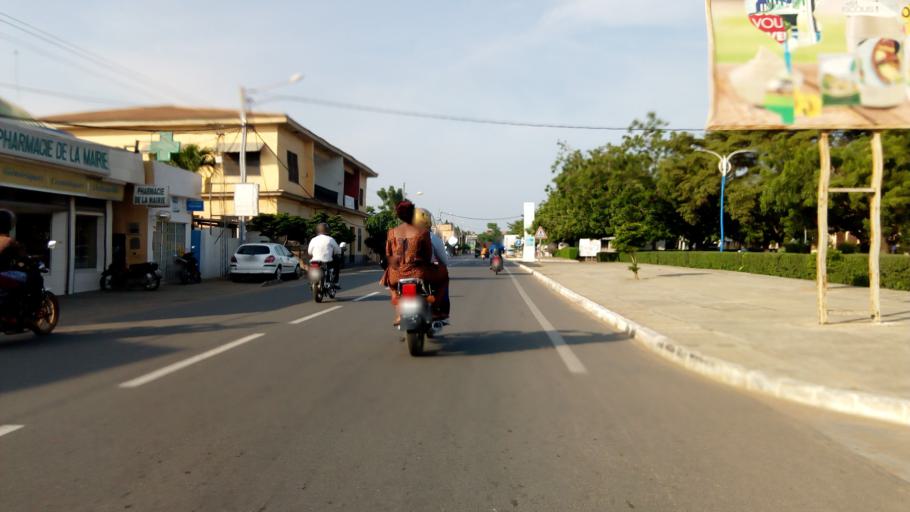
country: TG
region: Maritime
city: Lome
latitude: 6.1311
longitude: 1.2145
